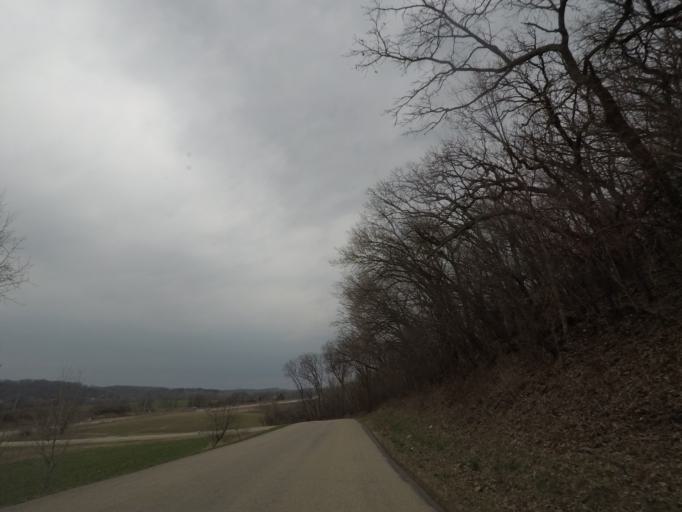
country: US
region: Wisconsin
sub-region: Dane County
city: Cross Plains
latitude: 43.0962
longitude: -89.6100
